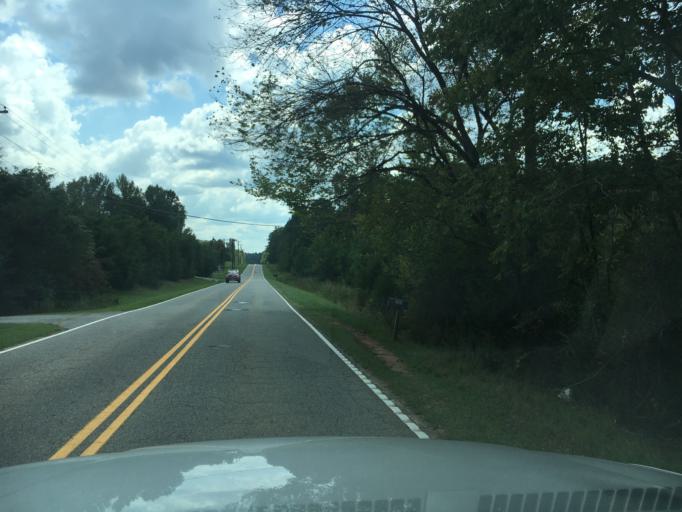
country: US
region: South Carolina
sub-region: Greenwood County
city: Greenwood
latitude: 34.1283
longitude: -82.1264
